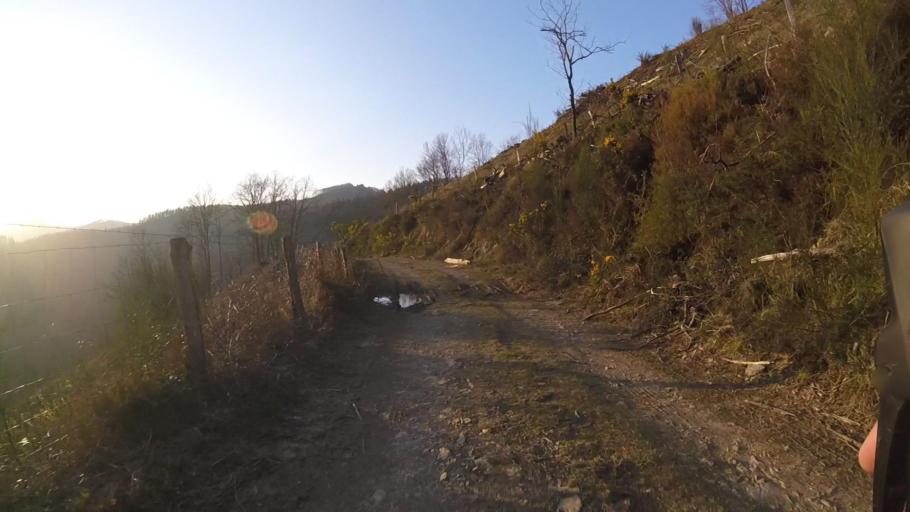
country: ES
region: Navarre
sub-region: Provincia de Navarra
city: Arano
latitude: 43.2491
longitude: -1.8584
